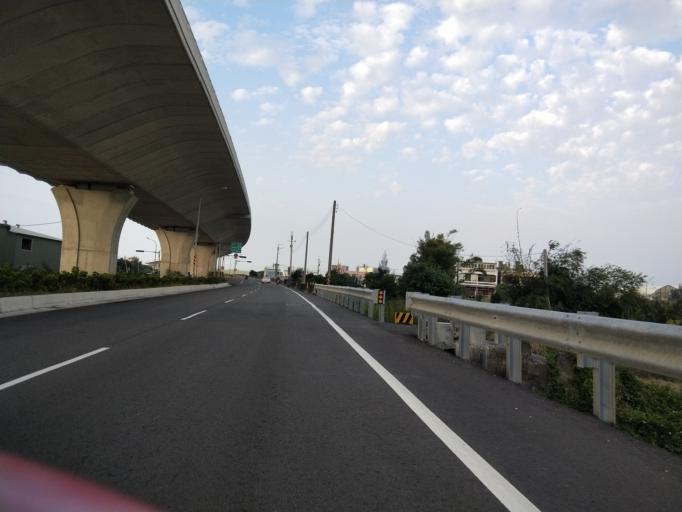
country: TW
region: Taiwan
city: Fengyuan
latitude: 24.4141
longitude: 120.6172
